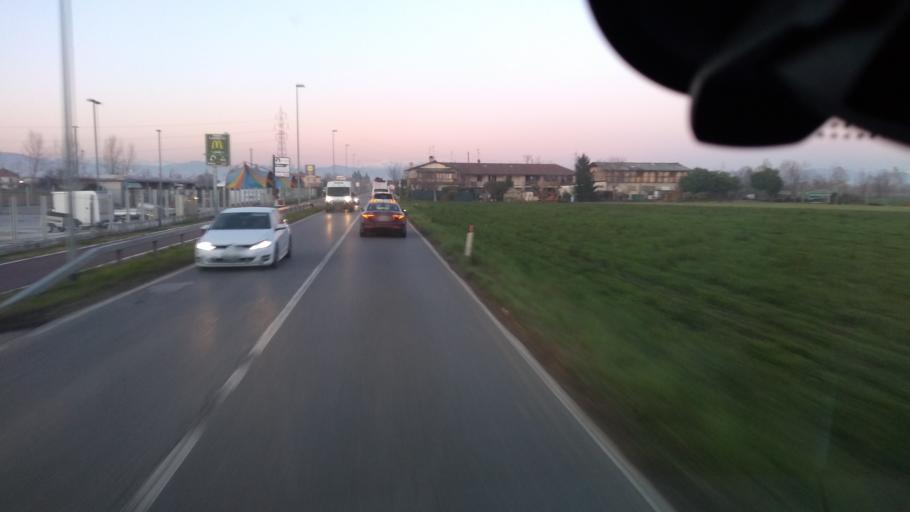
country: IT
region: Lombardy
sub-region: Provincia di Bergamo
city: Treviglio
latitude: 45.5369
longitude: 9.5991
